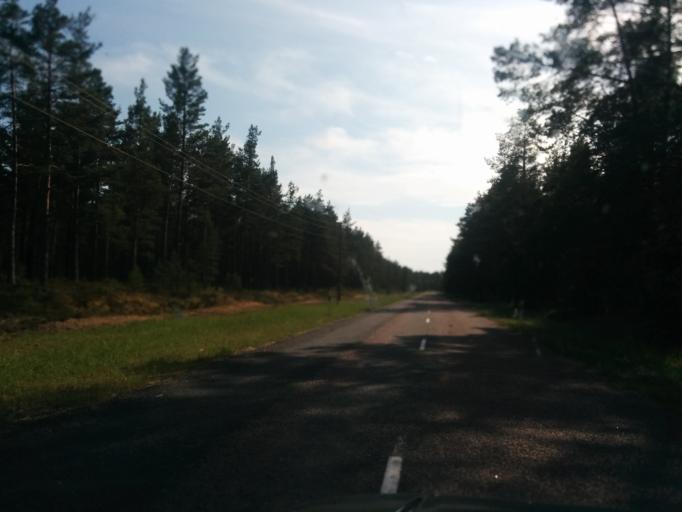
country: LV
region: Dundaga
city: Dundaga
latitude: 57.6591
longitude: 22.2850
